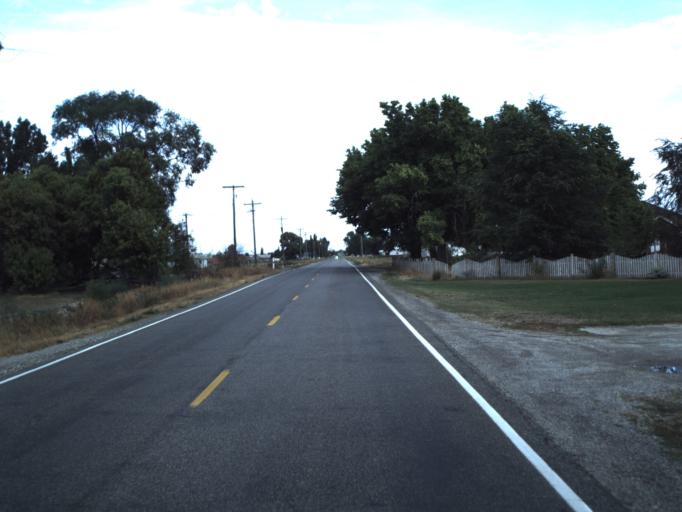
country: US
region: Utah
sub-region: Cache County
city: Lewiston
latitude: 41.9635
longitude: -111.9540
